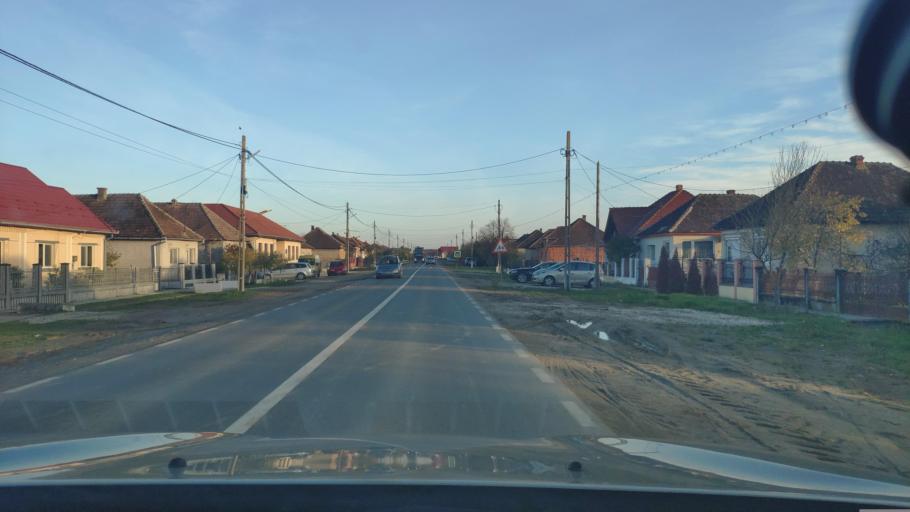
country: RO
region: Satu Mare
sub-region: Comuna Mediesu Aurit
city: Potau
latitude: 47.7761
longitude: 23.0967
